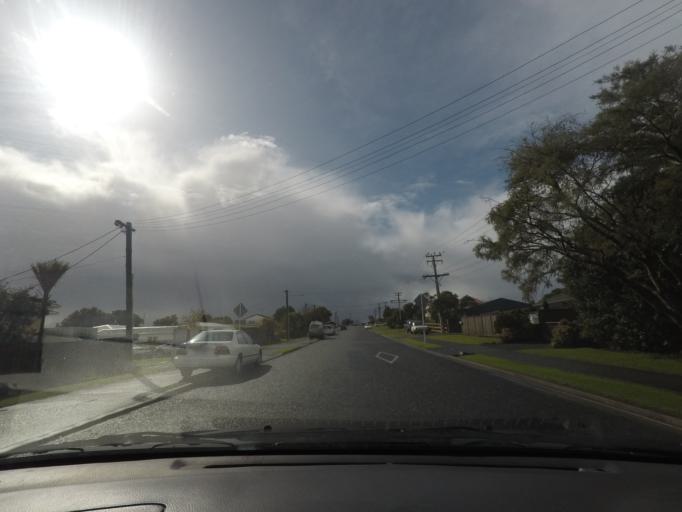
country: NZ
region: Auckland
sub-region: Auckland
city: Warkworth
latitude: -36.4278
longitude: 174.7265
